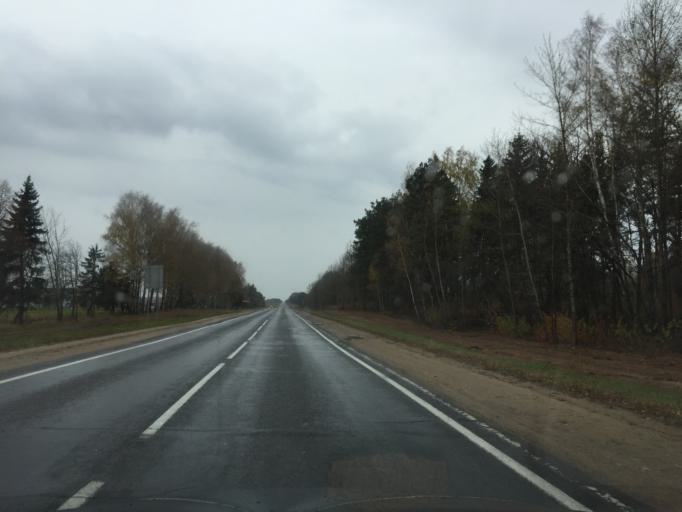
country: BY
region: Mogilev
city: Slawharad
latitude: 53.3988
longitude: 30.9183
